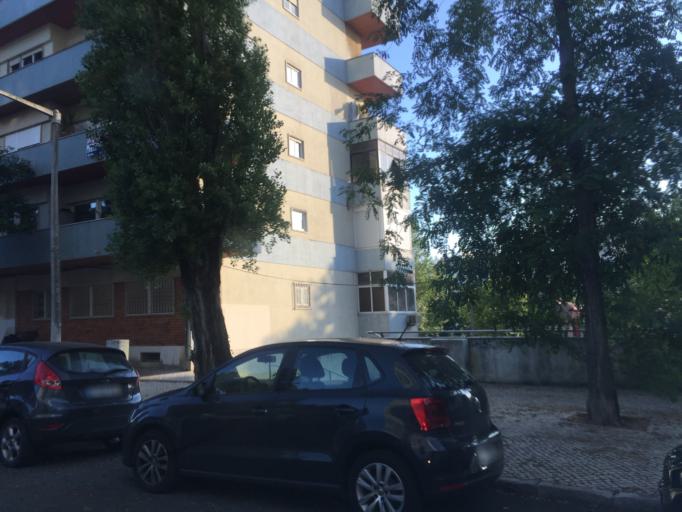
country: PT
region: Lisbon
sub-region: Odivelas
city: Pontinha
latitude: 38.7478
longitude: -9.2061
